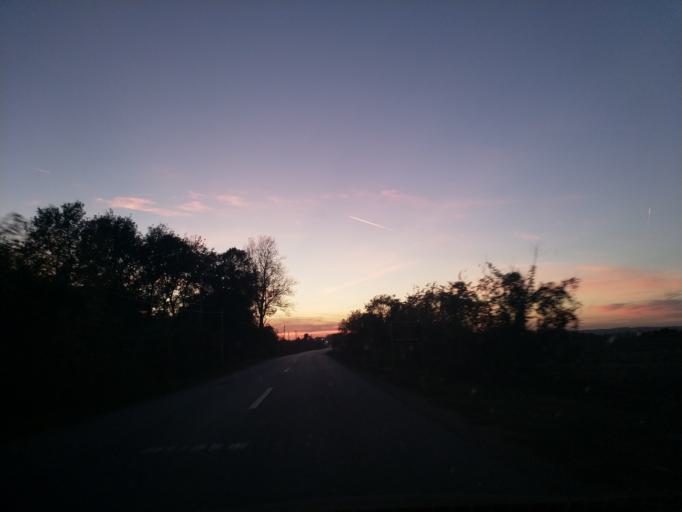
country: RS
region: Central Serbia
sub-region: Sumadijski Okrug
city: Lapovo
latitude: 44.2377
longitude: 21.1299
